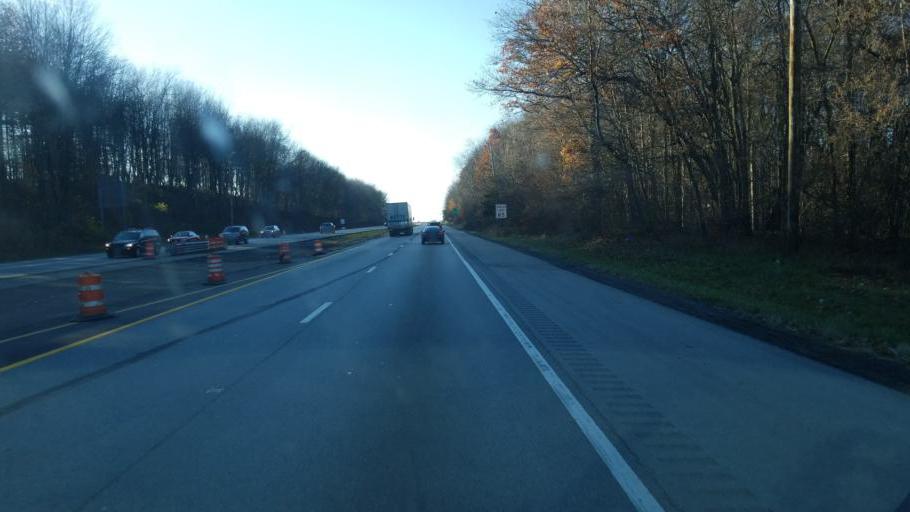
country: US
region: Ohio
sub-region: Medina County
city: Wadsworth
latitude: 41.0474
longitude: -81.7033
